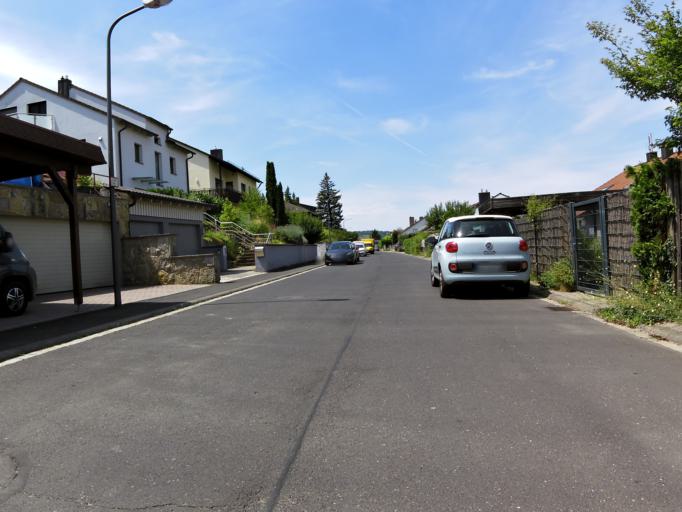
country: DE
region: Bavaria
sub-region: Regierungsbezirk Unterfranken
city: Randersacker
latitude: 49.7584
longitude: 9.9605
